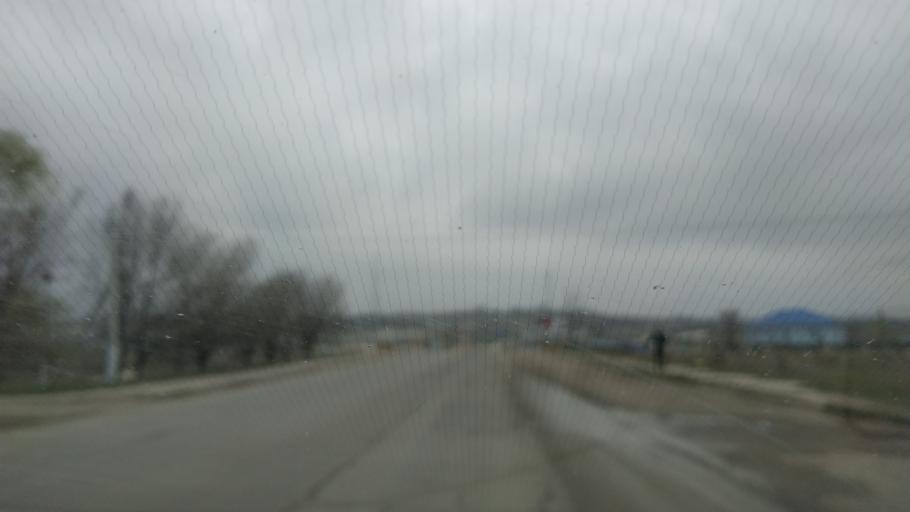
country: MD
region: Gagauzia
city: Comrat
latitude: 46.2945
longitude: 28.6619
